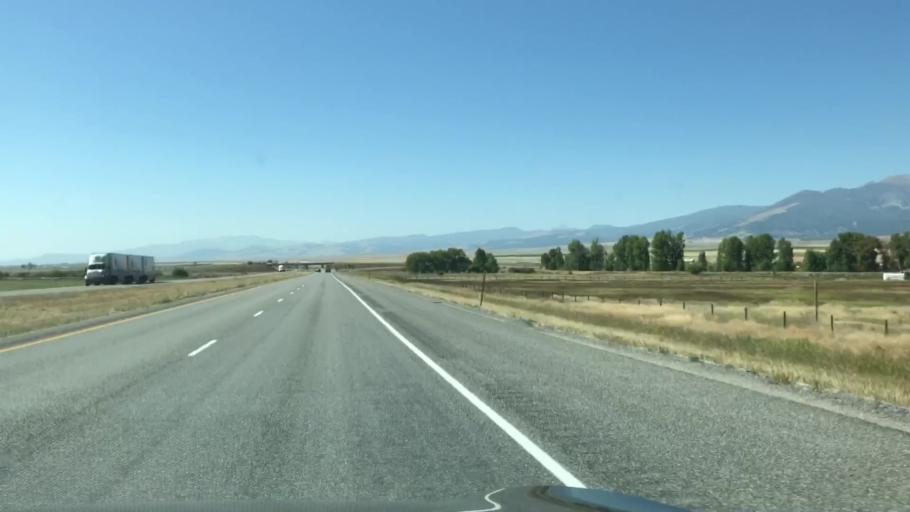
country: US
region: Montana
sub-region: Powell County
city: Deer Lodge
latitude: 46.3811
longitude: -112.7302
